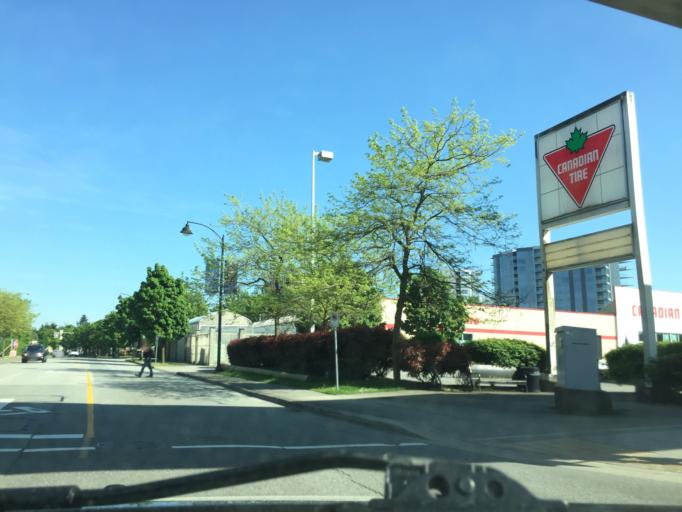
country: CA
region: British Columbia
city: Richmond
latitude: 49.1889
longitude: -123.1325
